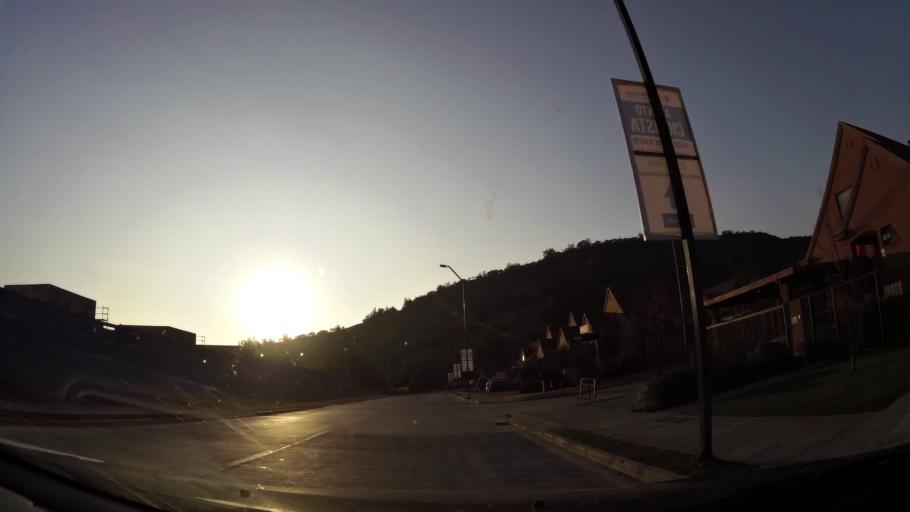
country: CL
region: Santiago Metropolitan
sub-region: Provincia de Chacabuco
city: Chicureo Abajo
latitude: -33.3226
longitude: -70.5170
